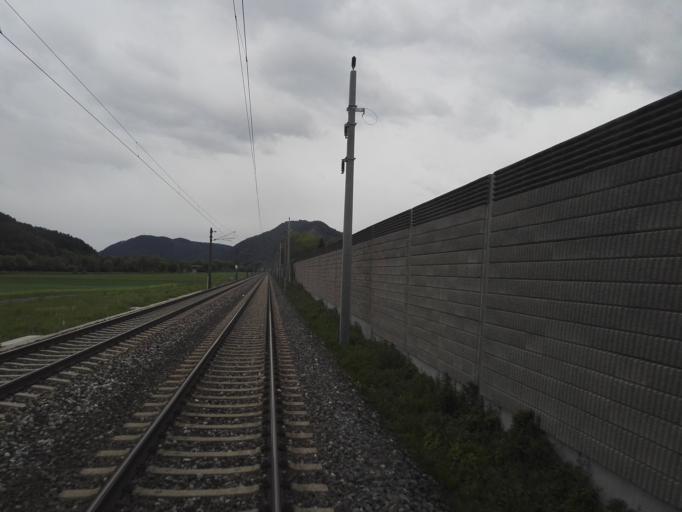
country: AT
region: Styria
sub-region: Politischer Bezirk Graz-Umgebung
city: Deutschfeistritz
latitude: 47.1928
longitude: 15.3373
